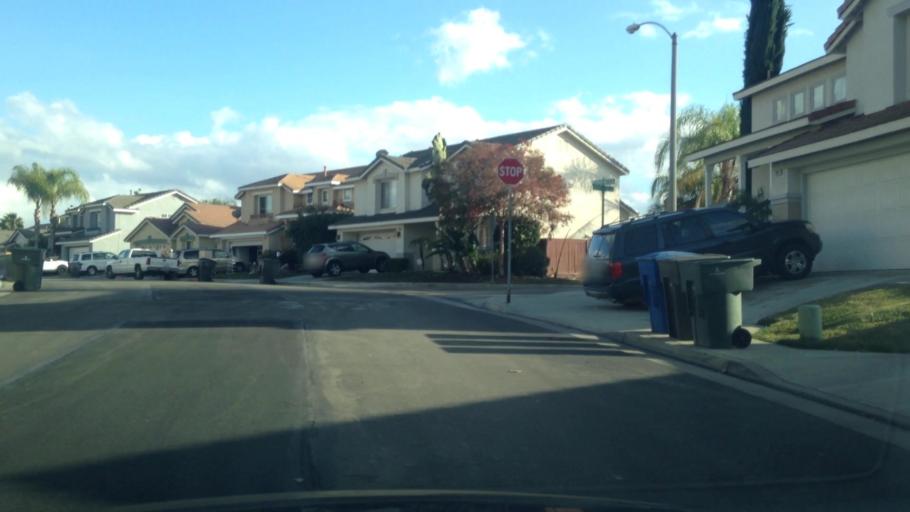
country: US
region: California
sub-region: Riverside County
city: Woodcrest
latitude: 33.9123
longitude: -117.3220
